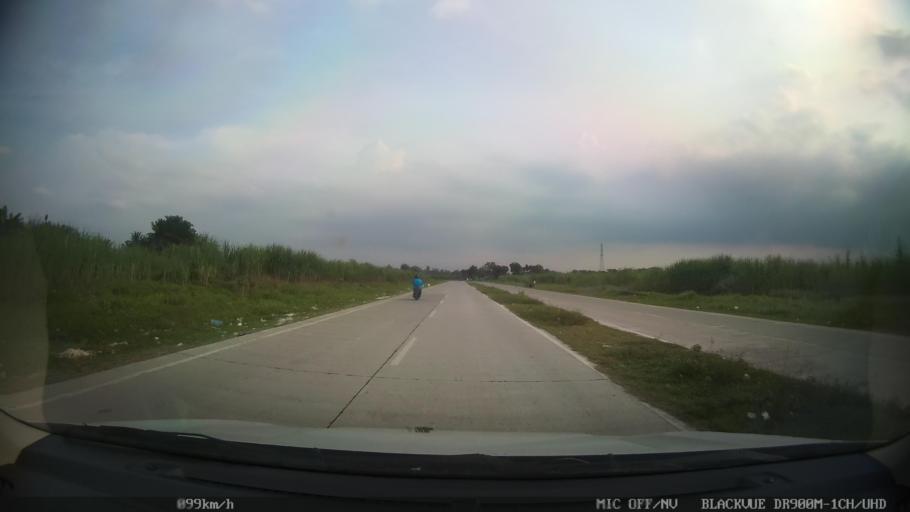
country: ID
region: North Sumatra
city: Binjai
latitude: 3.5961
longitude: 98.5330
